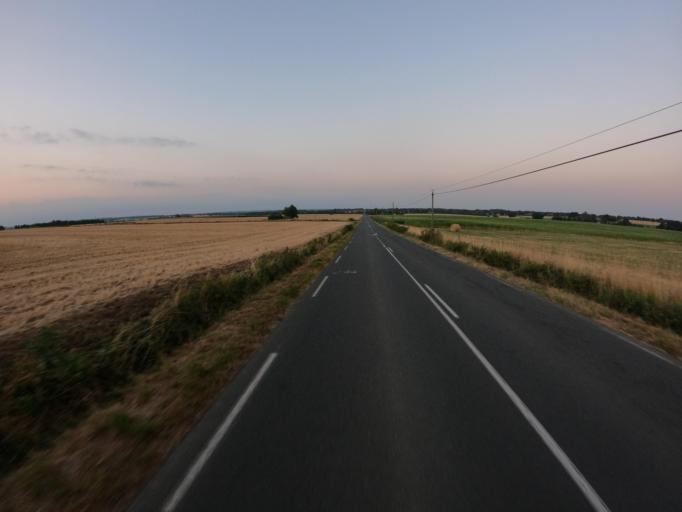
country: FR
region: Pays de la Loire
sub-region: Departement de Maine-et-Loire
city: Noyant-la-Gravoyere
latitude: 47.6486
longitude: -0.9379
